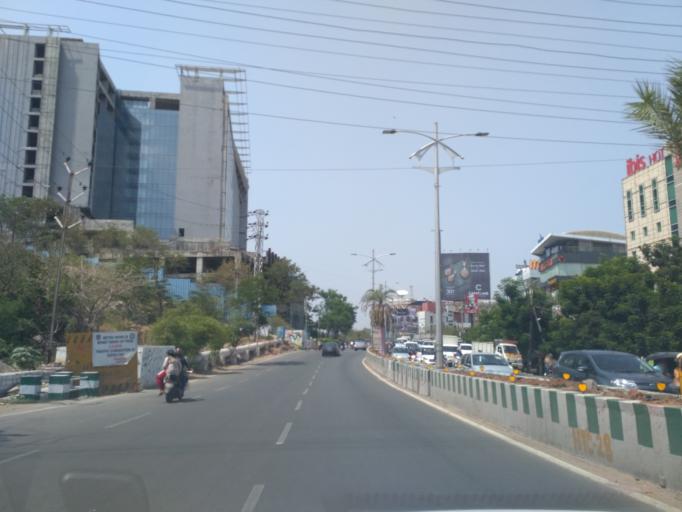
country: IN
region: Telangana
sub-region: Rangareddi
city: Kukatpalli
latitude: 17.4472
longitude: 78.3780
